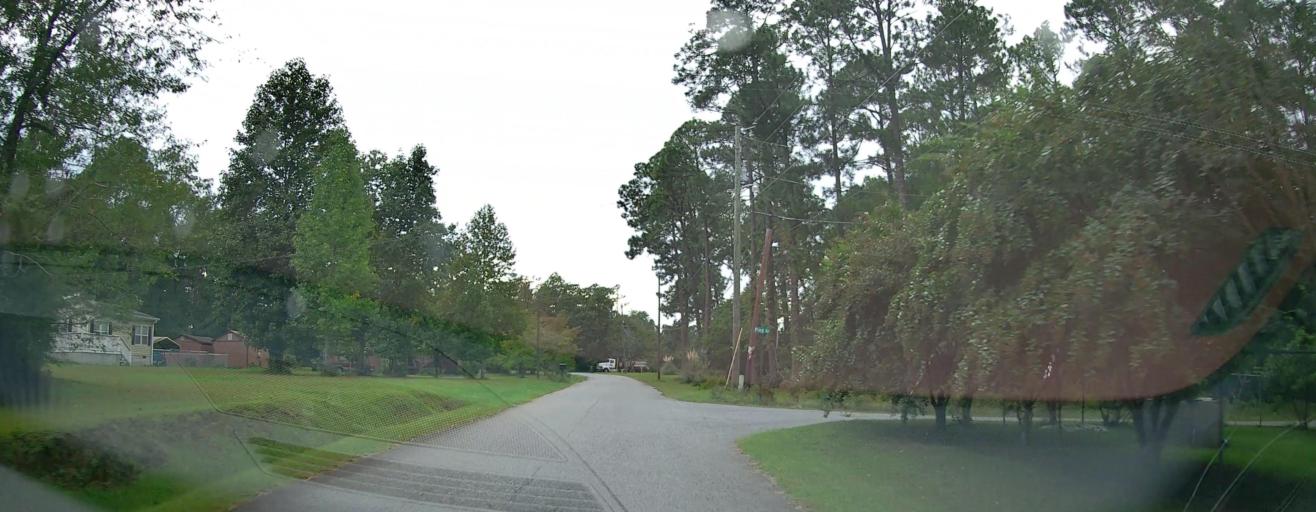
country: US
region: Georgia
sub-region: Peach County
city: Byron
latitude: 32.6760
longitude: -83.7142
